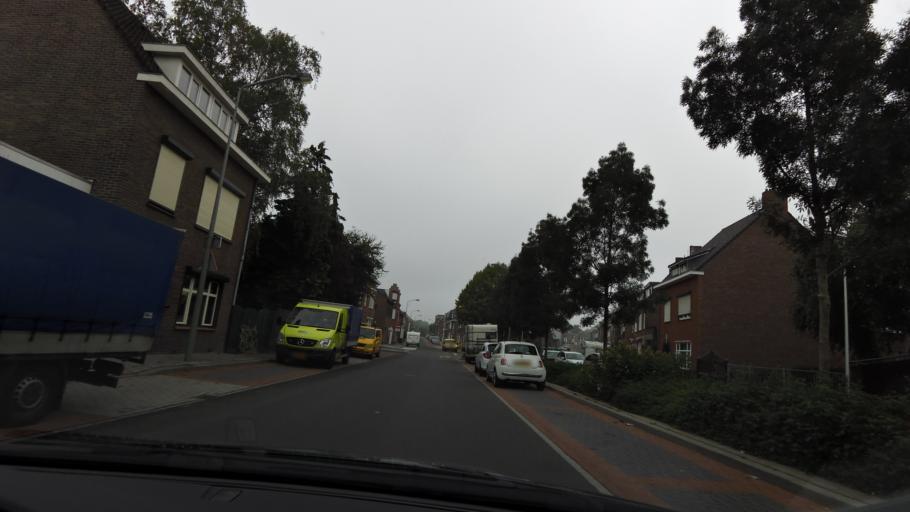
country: NL
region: Limburg
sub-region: Gemeente Brunssum
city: Brunssum
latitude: 50.9147
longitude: 5.9642
